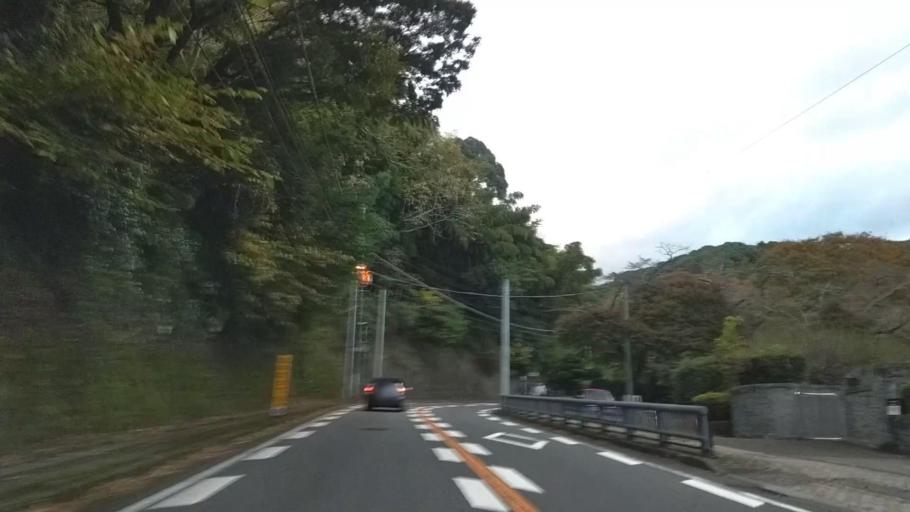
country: JP
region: Shizuoka
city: Atami
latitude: 35.0984
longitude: 139.0577
